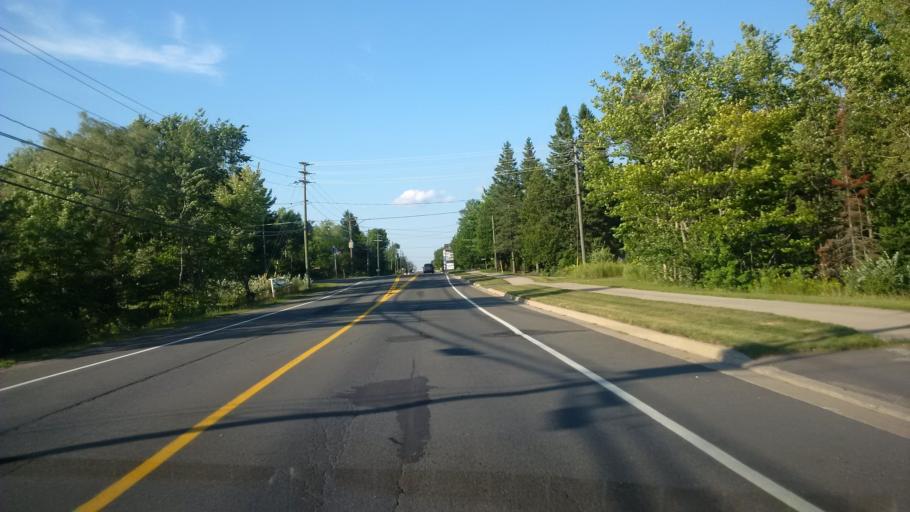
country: CA
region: New Brunswick
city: Fredericton
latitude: 45.8862
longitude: -66.6879
